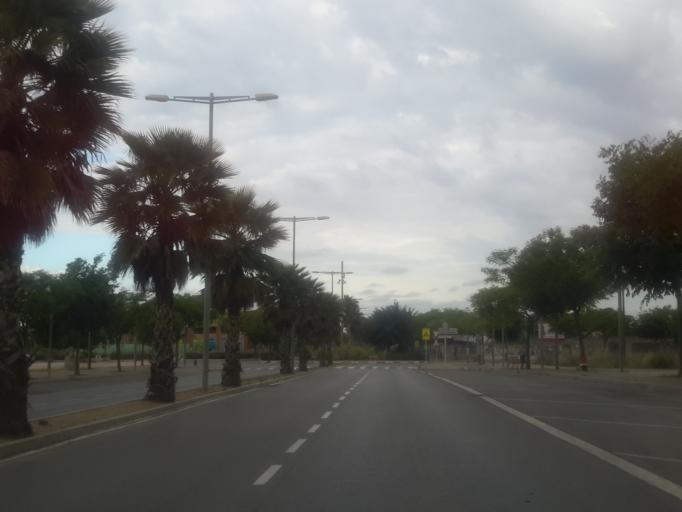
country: ES
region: Catalonia
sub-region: Provincia de Barcelona
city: Vilanova i la Geltru
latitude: 41.2357
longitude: 1.7503
